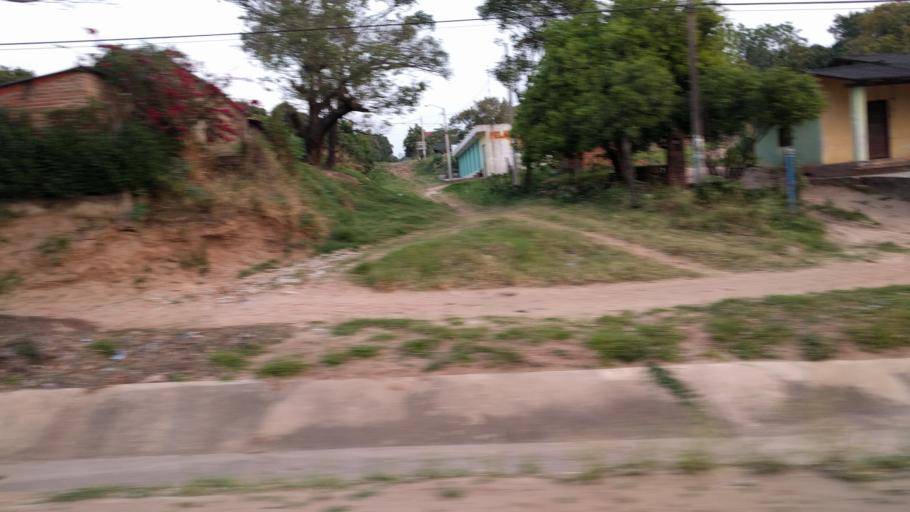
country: BO
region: Santa Cruz
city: Santa Rita
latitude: -17.8937
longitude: -63.3333
